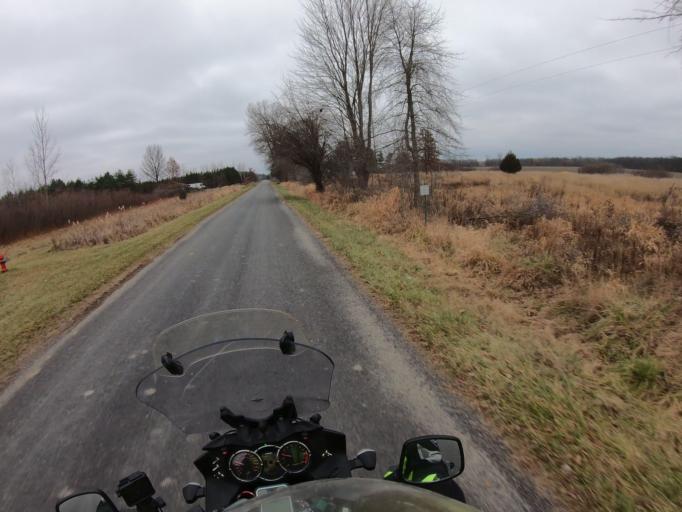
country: US
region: Michigan
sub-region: Saginaw County
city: Saint Charles
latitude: 43.3320
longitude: -84.1316
